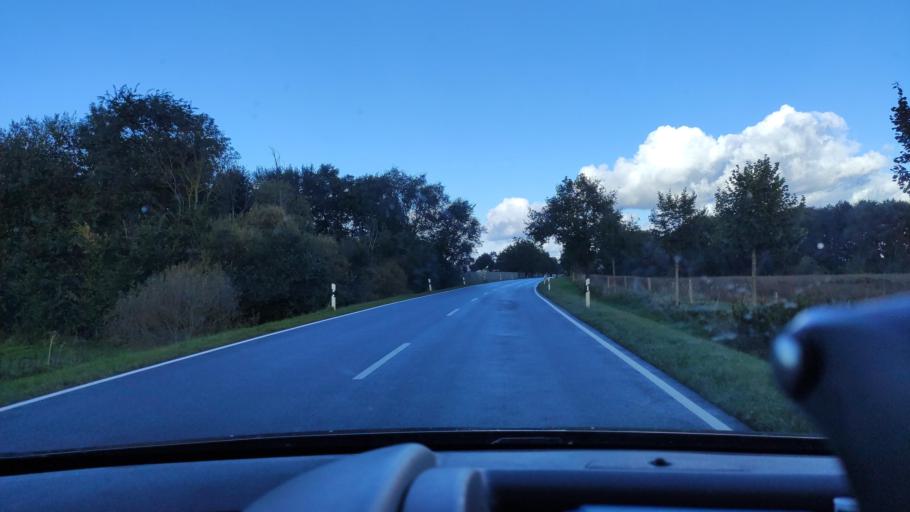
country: DE
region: Mecklenburg-Vorpommern
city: Tarnow
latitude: 53.7599
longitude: 12.0440
